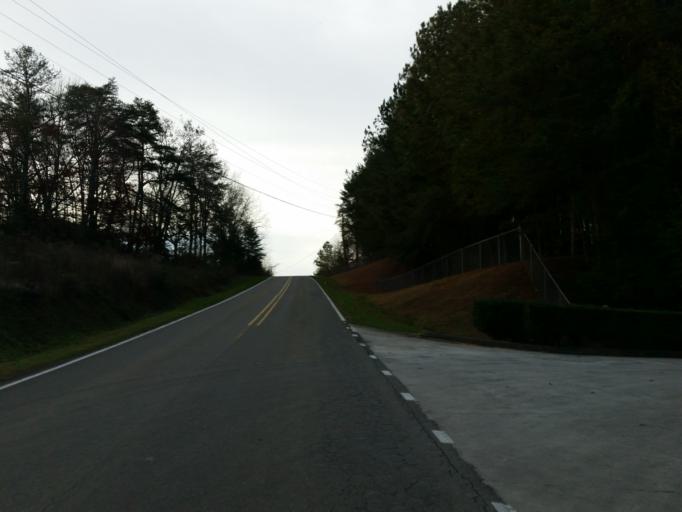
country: US
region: Georgia
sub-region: Pickens County
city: Jasper
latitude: 34.4488
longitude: -84.4526
